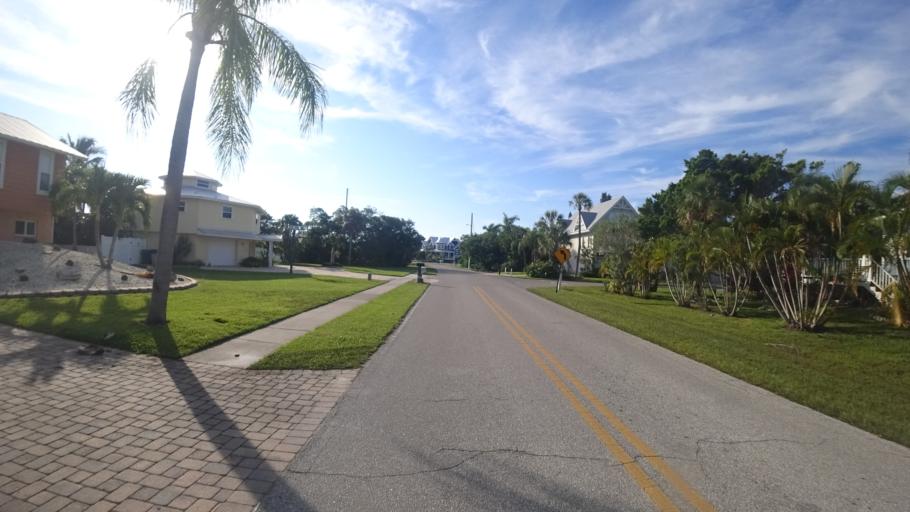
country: US
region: Florida
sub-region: Manatee County
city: Anna Maria
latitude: 27.5211
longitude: -82.7248
